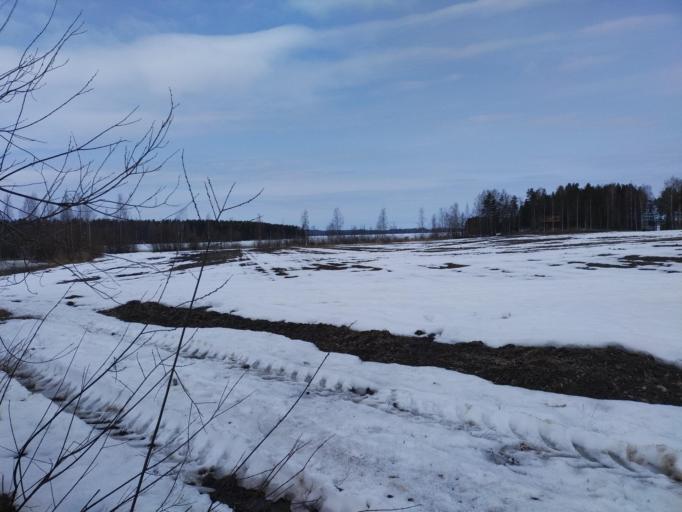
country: FI
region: Southern Savonia
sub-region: Savonlinna
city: Punkaharju
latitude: 61.6713
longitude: 29.2911
